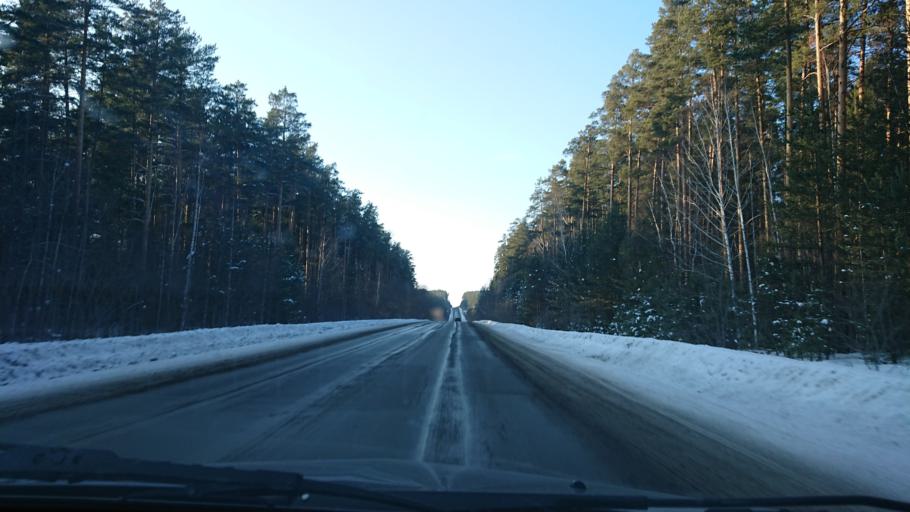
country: RU
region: Sverdlovsk
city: Gornyy Shchit
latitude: 56.6315
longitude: 60.3294
